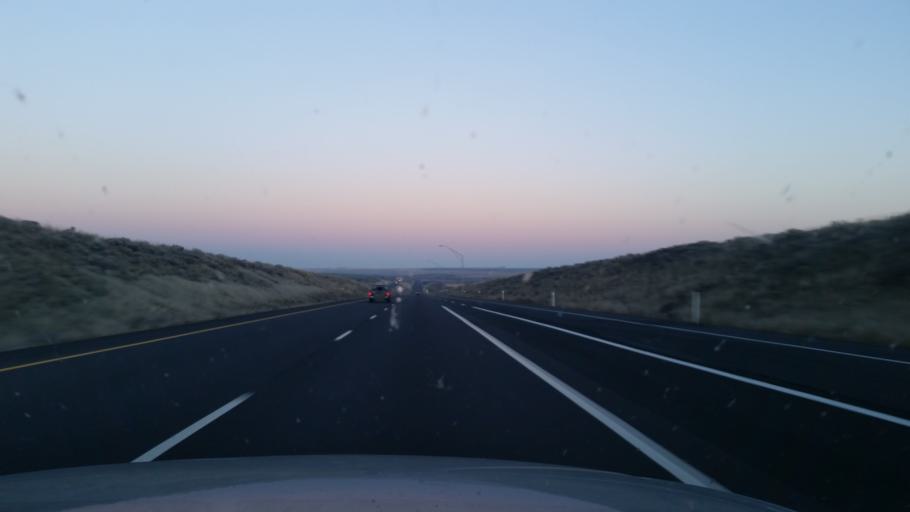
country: US
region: Washington
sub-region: Adams County
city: Ritzville
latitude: 47.0968
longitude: -118.6606
